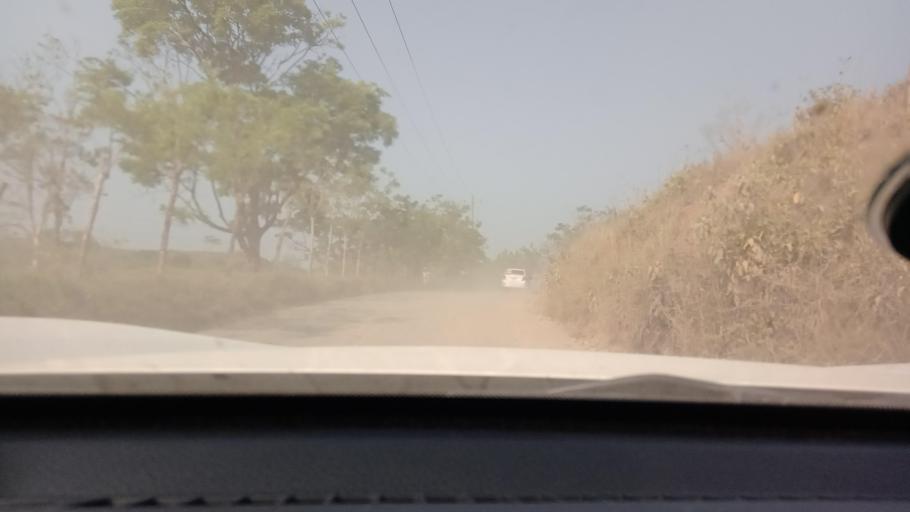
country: MX
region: Tabasco
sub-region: Huimanguillo
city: Francisco Rueda
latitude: 17.6494
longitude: -93.9035
